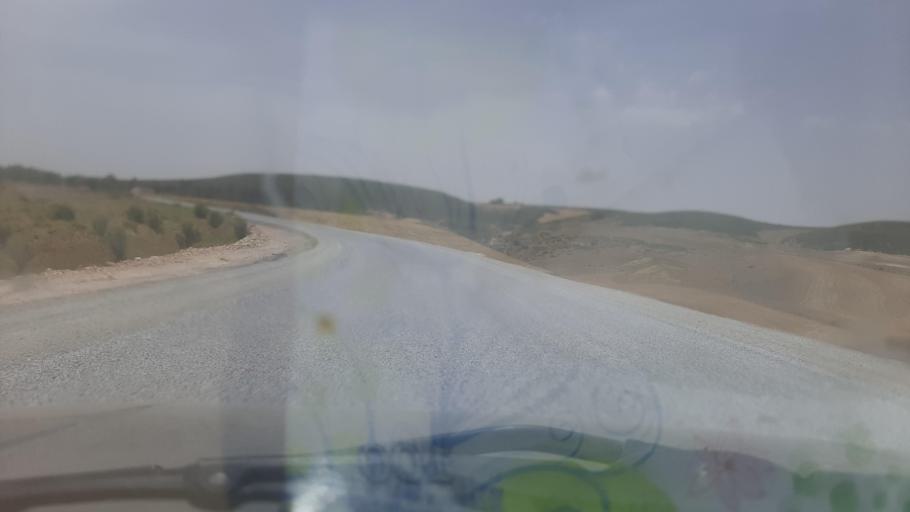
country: TN
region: Tunis
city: La Mohammedia
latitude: 36.5470
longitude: 10.1522
